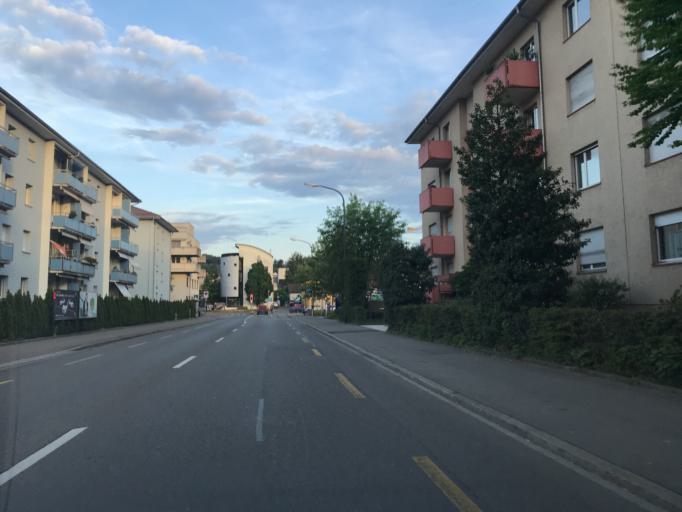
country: CH
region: Zurich
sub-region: Bezirk Winterthur
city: Toess (Kreis 4) / Schlosstal
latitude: 47.4939
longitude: 8.7078
